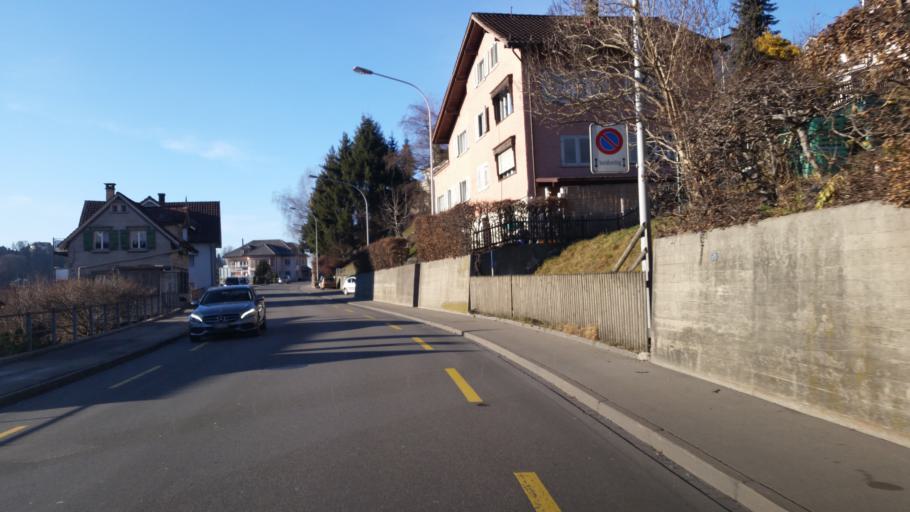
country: CH
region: Appenzell Ausserrhoden
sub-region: Bezirk Hinterland
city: Herisau
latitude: 47.3930
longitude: 9.2700
